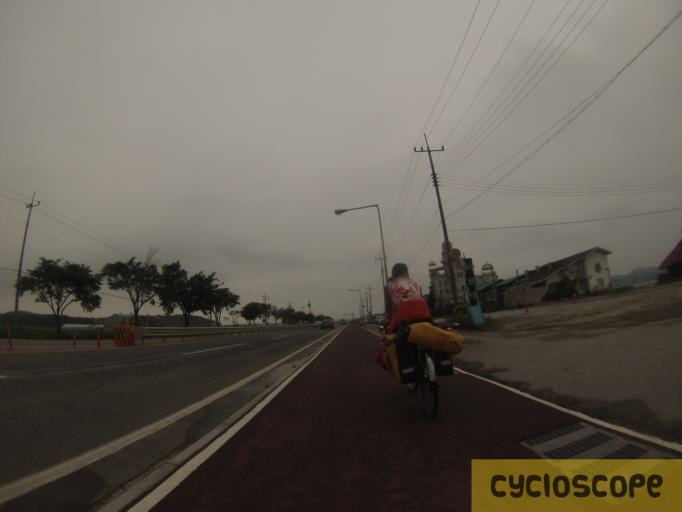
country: KR
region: Chungcheongnam-do
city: Taisen-ri
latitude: 36.1632
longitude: 126.5232
